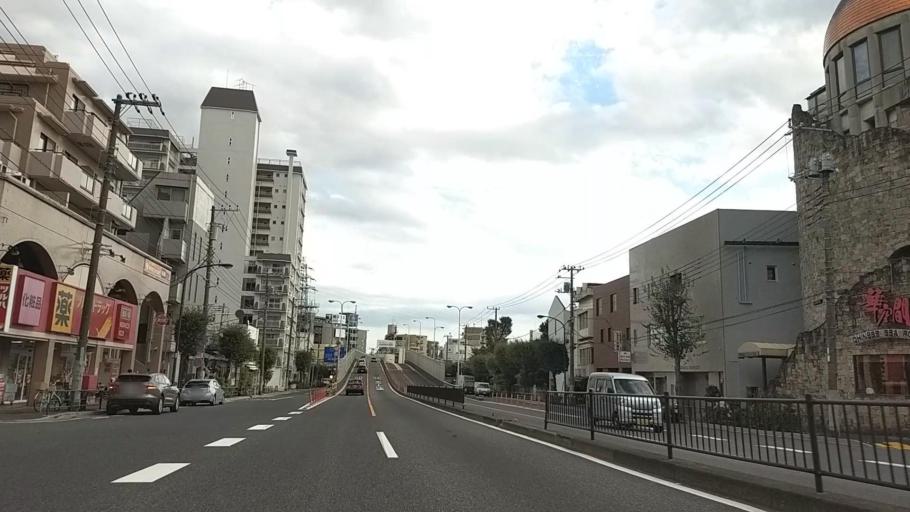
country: JP
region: Tokyo
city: Tokyo
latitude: 35.6283
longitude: 139.6753
